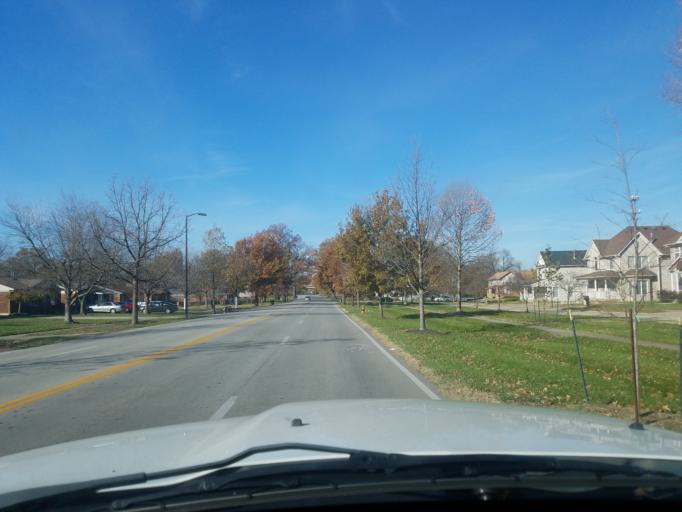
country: US
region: Kentucky
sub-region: Jefferson County
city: Shively
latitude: 38.2253
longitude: -85.8169
